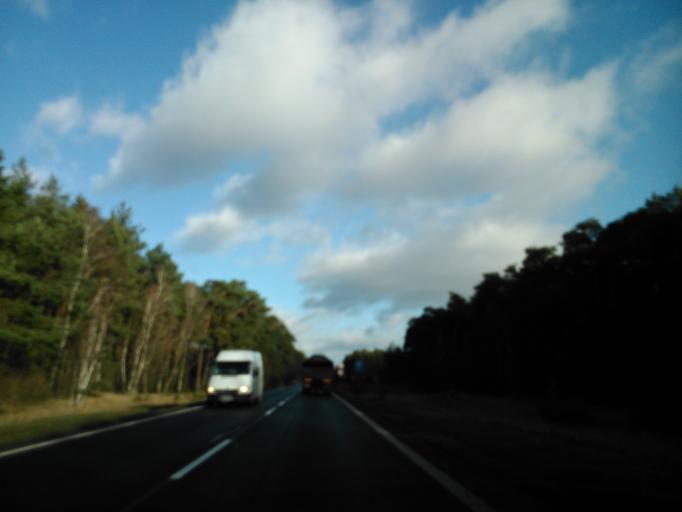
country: PL
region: Kujawsko-Pomorskie
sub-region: Powiat torunski
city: Wielka Nieszawka
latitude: 52.9522
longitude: 18.5287
